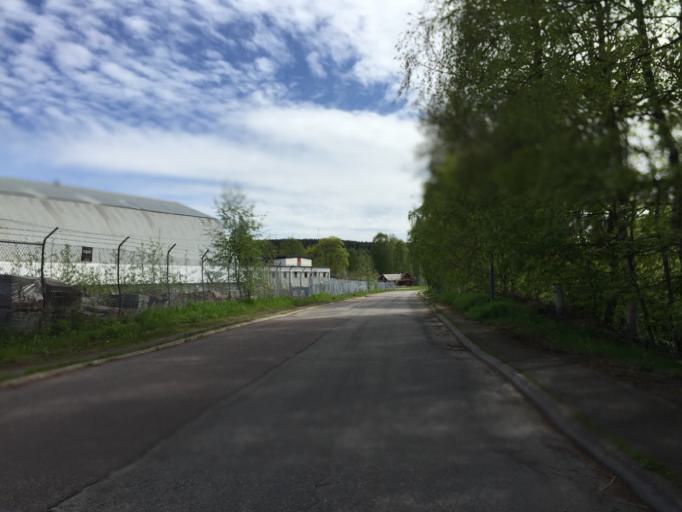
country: SE
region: Dalarna
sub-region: Ludvika Kommun
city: Ludvika
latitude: 60.1356
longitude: 15.1650
